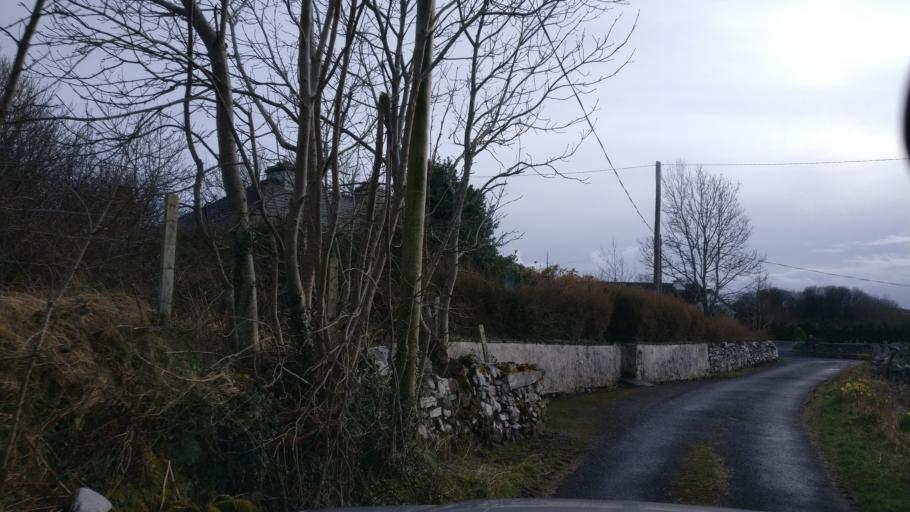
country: IE
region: Connaught
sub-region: County Galway
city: Oughterard
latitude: 53.5581
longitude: -9.4386
